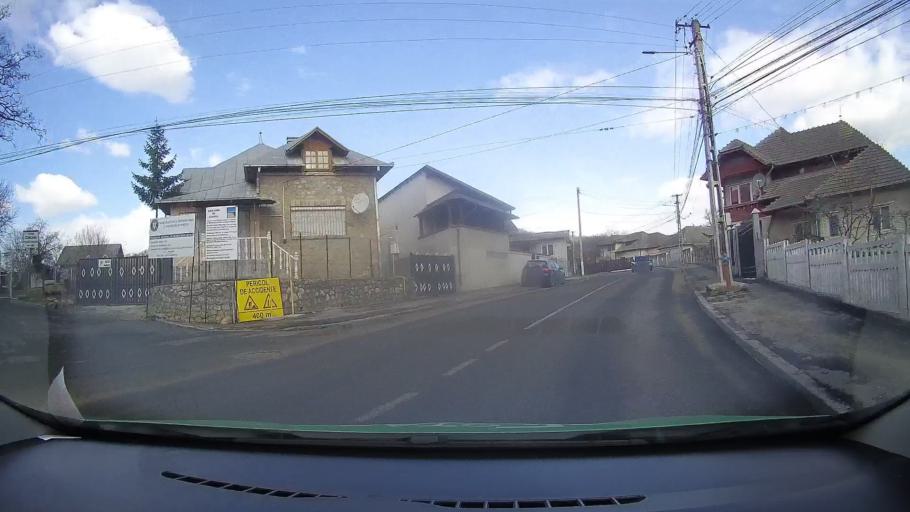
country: RO
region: Dambovita
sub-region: Comuna Fieni
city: Fieni
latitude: 45.1267
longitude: 25.4183
